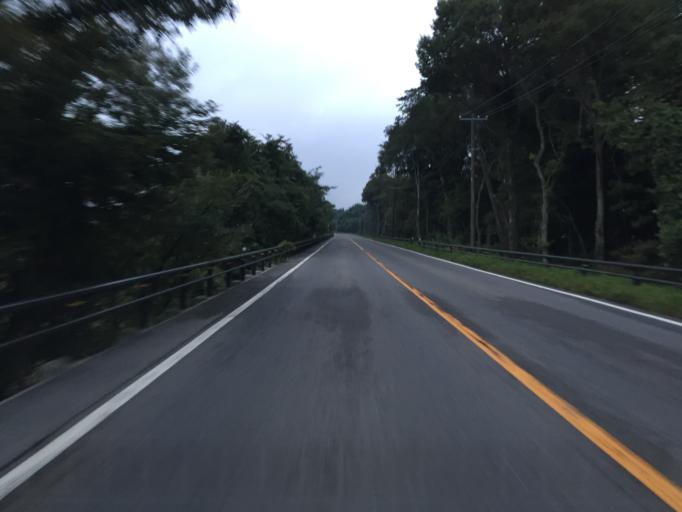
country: JP
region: Fukushima
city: Inawashiro
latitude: 37.5140
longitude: 140.0275
